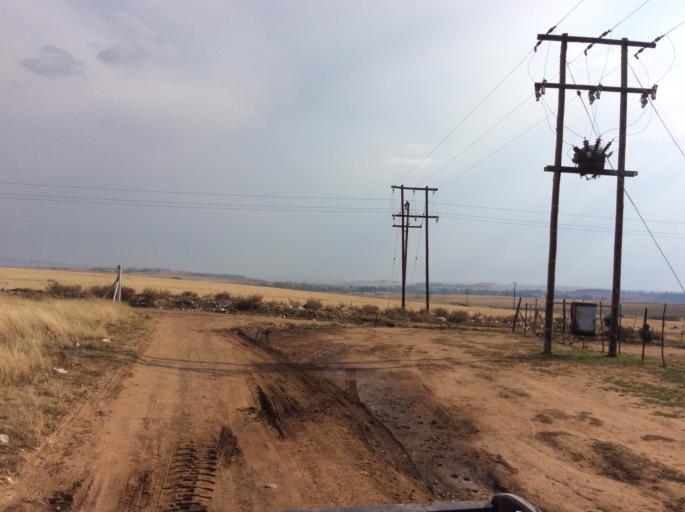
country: LS
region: Mafeteng
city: Mafeteng
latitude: -29.7146
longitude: 27.0106
